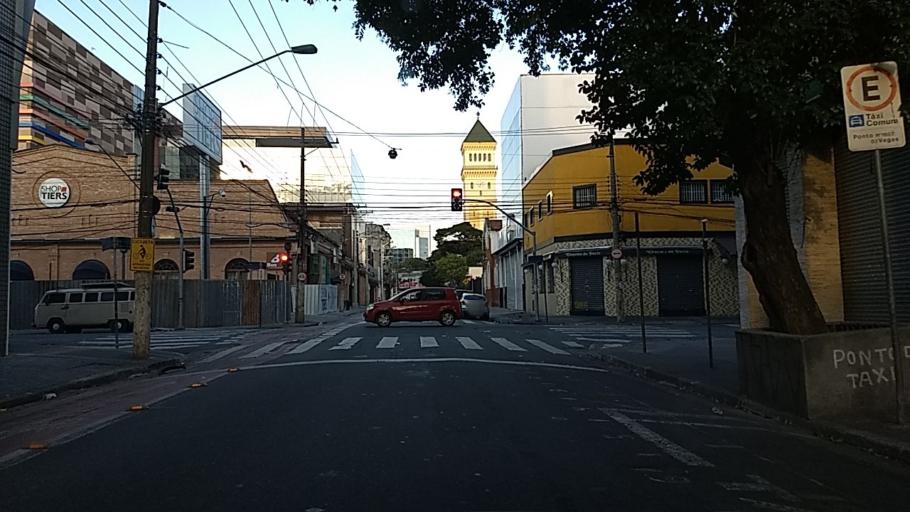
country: BR
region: Sao Paulo
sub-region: Sao Paulo
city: Sao Paulo
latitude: -23.5317
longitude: -46.6207
